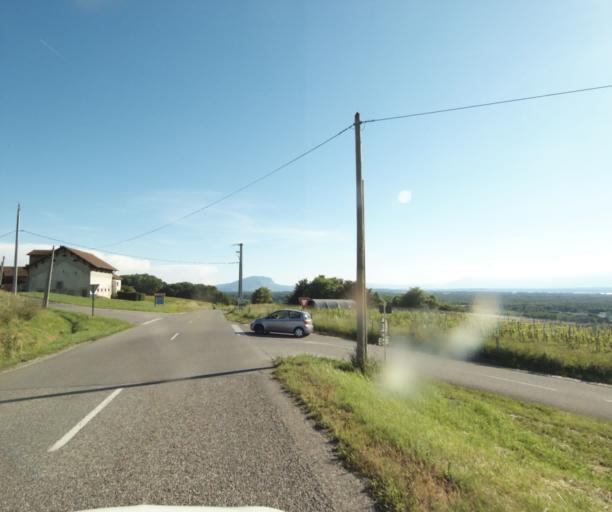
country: FR
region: Rhone-Alpes
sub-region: Departement de la Haute-Savoie
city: Ballaison
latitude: 46.2975
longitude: 6.3215
